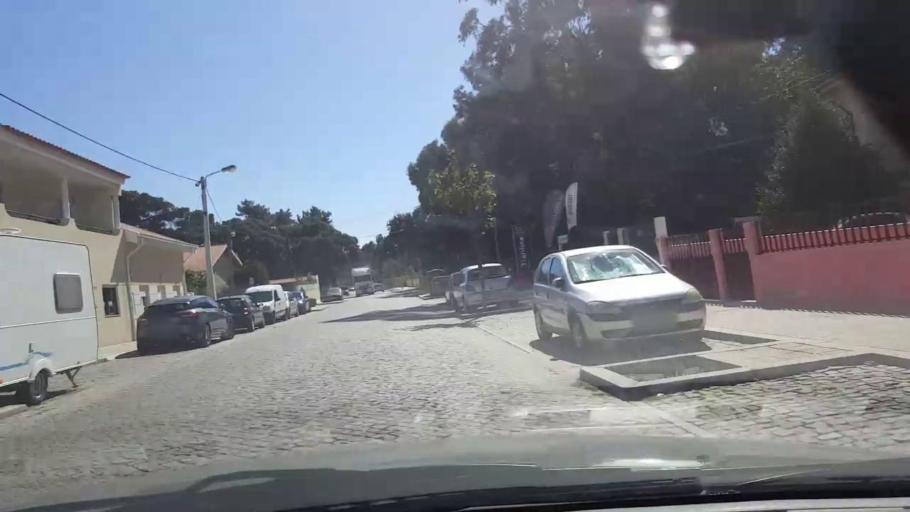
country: PT
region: Porto
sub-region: Vila do Conde
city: Arvore
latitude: 41.3321
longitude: -8.7307
